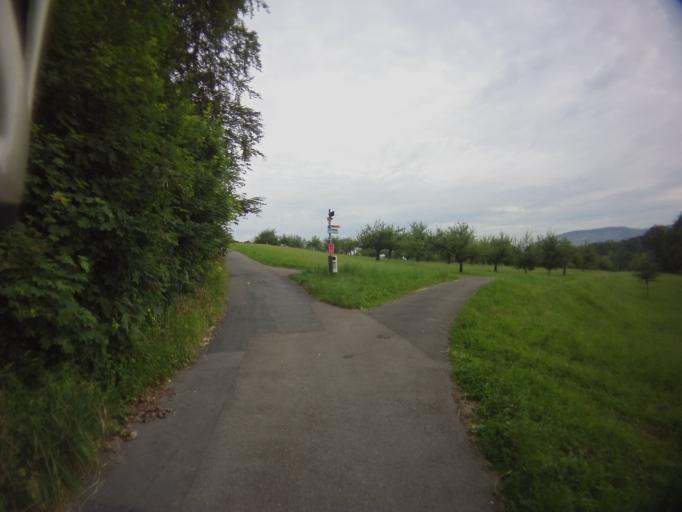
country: CH
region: Zurich
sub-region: Bezirk Zuerich
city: Zuerich (Kreis 2) / Unter-Leimbach
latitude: 47.3387
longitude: 8.5138
